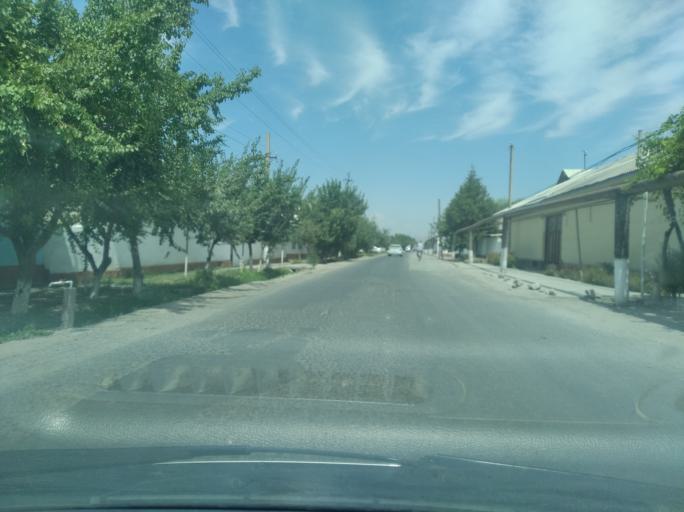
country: KG
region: Osh
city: Aravan
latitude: 40.6077
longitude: 72.4584
